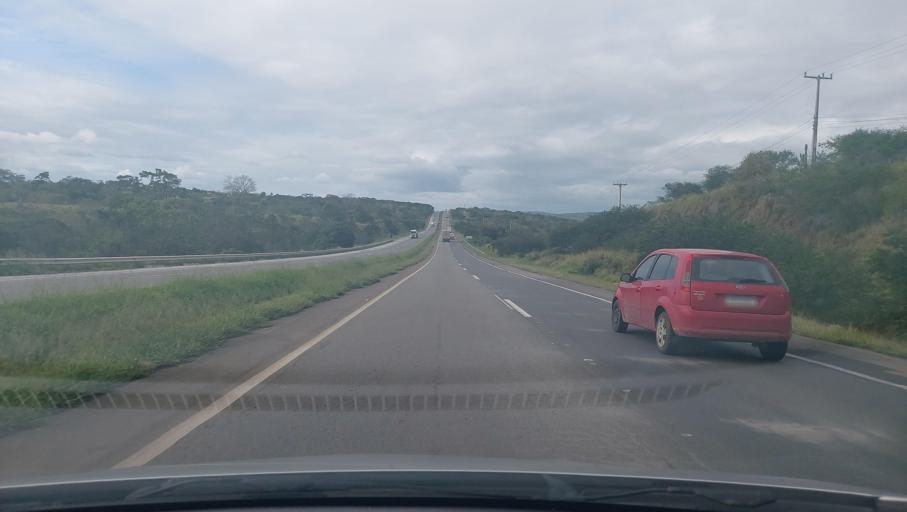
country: BR
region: Bahia
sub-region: Santo Estevao
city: Santo Estevao
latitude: -12.4326
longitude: -39.2165
